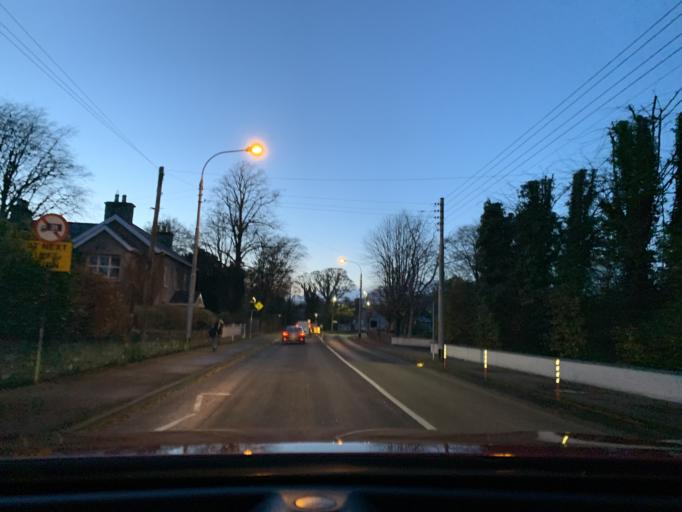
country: IE
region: Connaught
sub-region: Roscommon
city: Boyle
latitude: 53.9722
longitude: -8.2950
